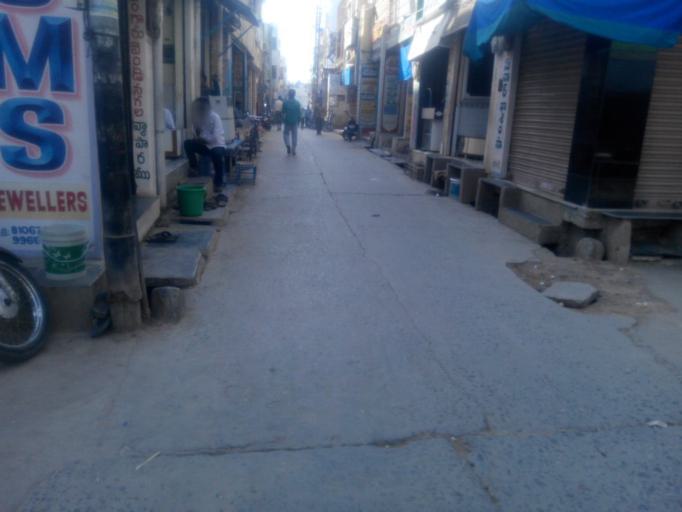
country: IN
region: Andhra Pradesh
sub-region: Kurnool
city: Nandyal
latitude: 15.4904
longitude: 78.4853
